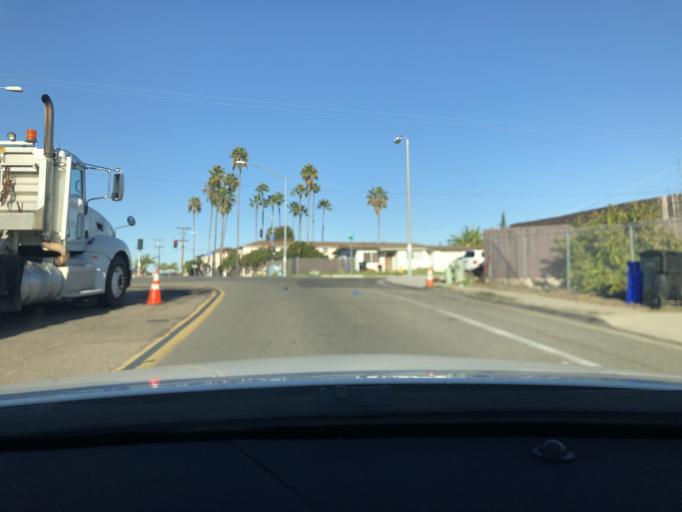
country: US
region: California
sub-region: San Diego County
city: Lemon Grove
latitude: 32.7449
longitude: -117.0591
